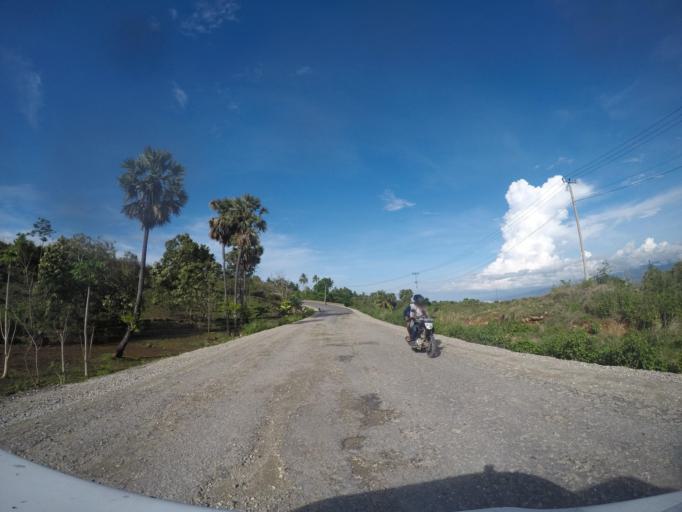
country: TL
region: Baucau
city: Baucau
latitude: -8.5065
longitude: 126.4443
